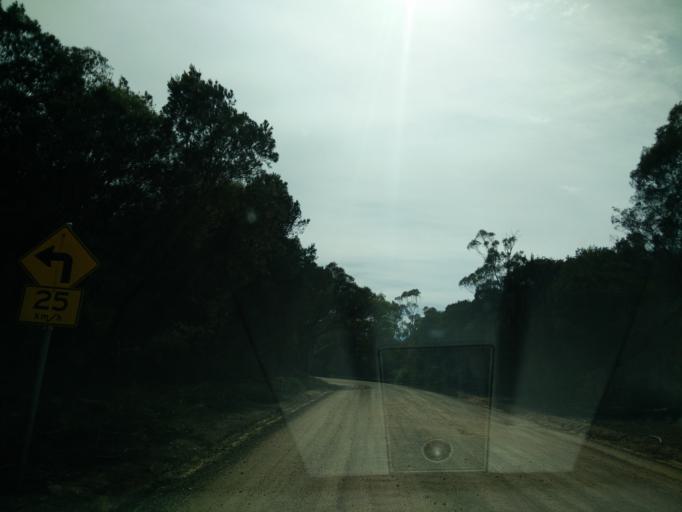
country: AU
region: Tasmania
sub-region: Break O'Day
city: St Helens
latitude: -42.0013
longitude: 148.2721
